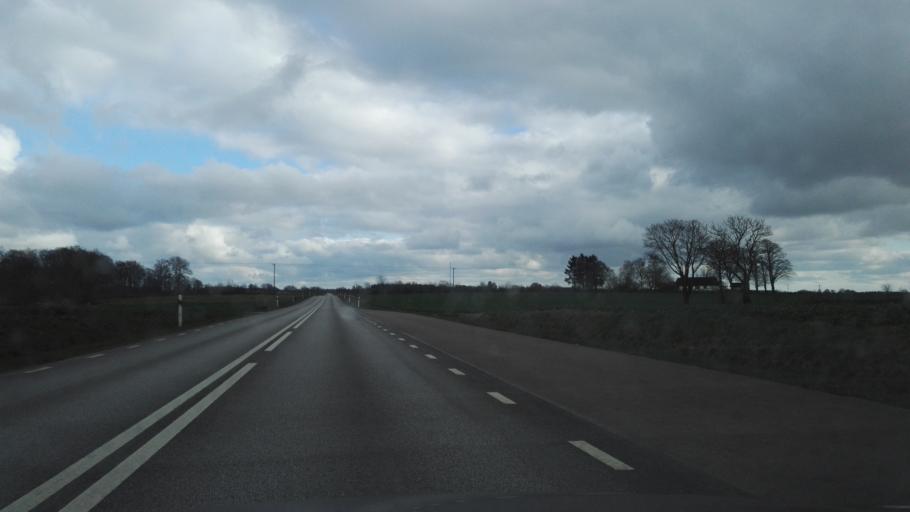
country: SE
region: Skane
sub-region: Horby Kommun
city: Hoerby
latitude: 55.7526
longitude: 13.6866
